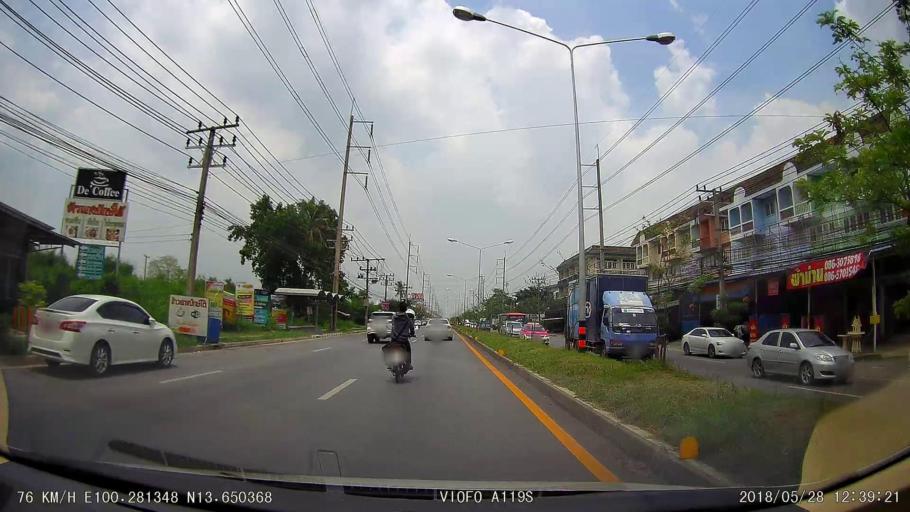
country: TH
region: Samut Sakhon
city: Krathum Baen
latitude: 13.6503
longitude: 100.2815
